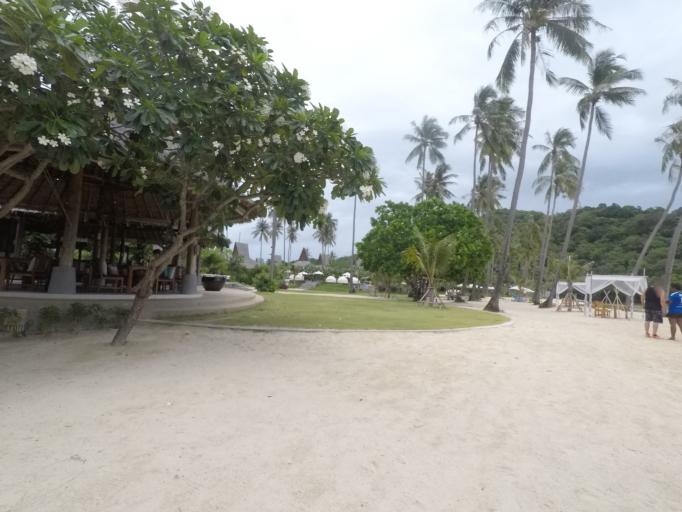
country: TH
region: Phangnga
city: Ban Phru Nai
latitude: 7.7617
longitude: 98.7726
